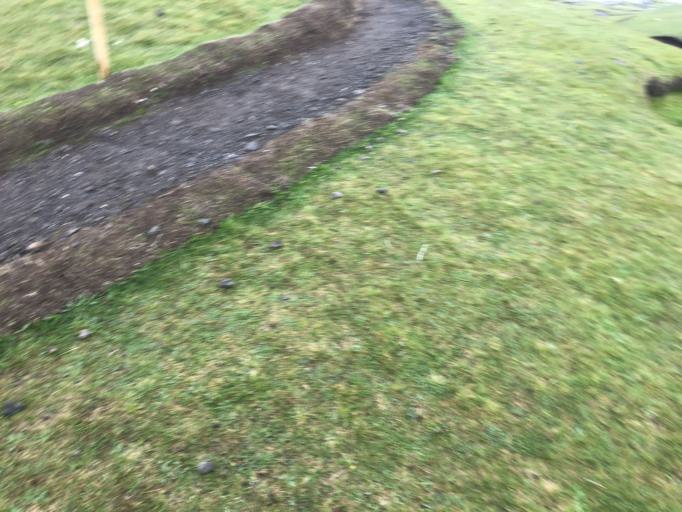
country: FO
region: Vagar
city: Midvagur
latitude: 62.0224
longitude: -7.2312
